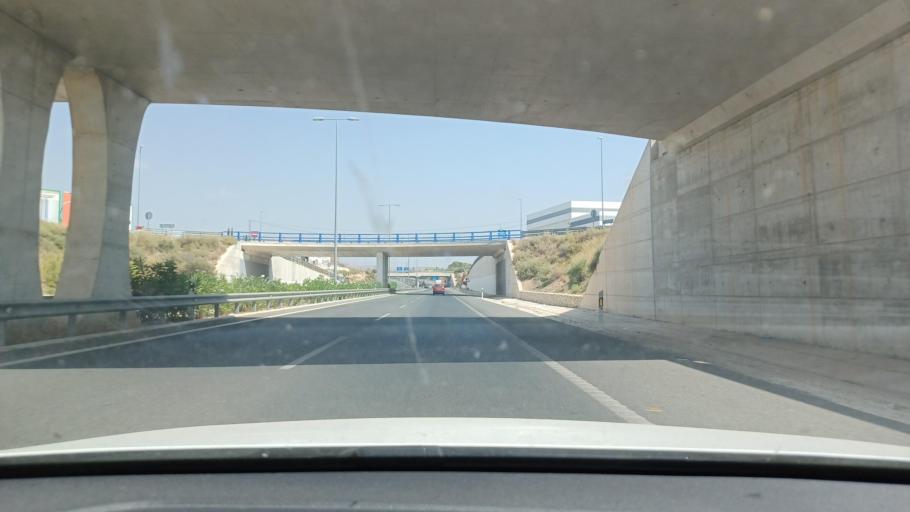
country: ES
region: Valencia
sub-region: Provincia de Alicante
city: Elche
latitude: 38.2743
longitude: -0.6612
